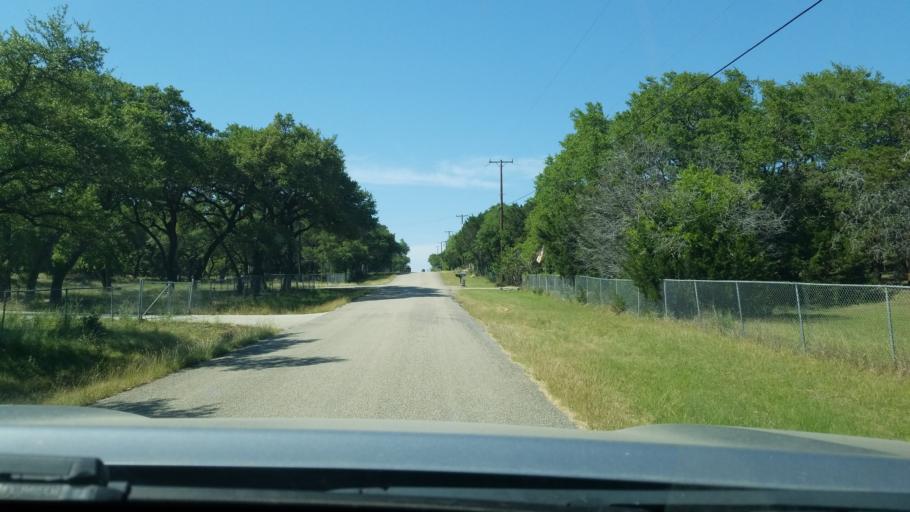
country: US
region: Texas
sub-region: Comal County
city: Bulverde
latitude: 29.7621
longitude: -98.5153
